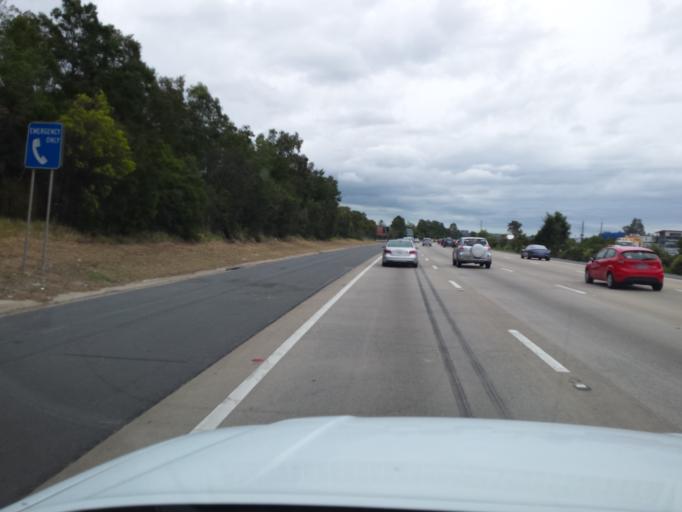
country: AU
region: Queensland
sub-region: Gold Coast
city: Oxenford
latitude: -27.8969
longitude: 153.3143
